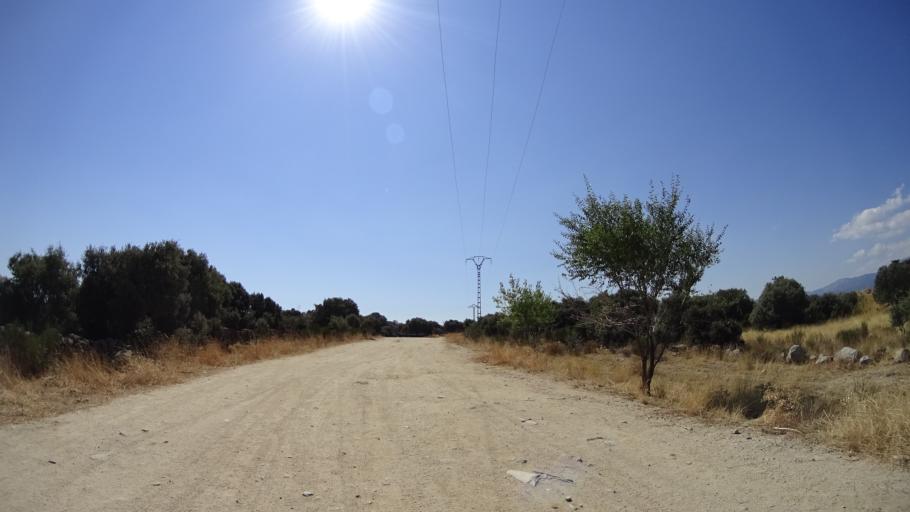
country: ES
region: Madrid
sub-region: Provincia de Madrid
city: Collado-Villalba
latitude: 40.6117
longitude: -4.0110
